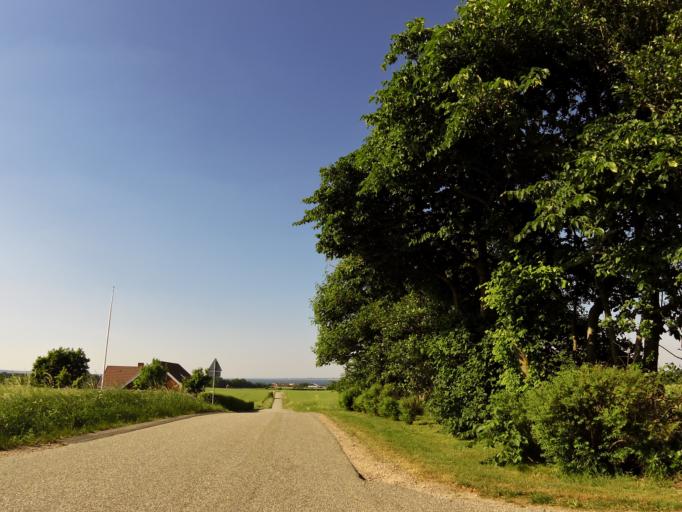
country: DK
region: Central Jutland
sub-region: Holstebro Kommune
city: Vinderup
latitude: 56.4612
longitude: 8.6999
